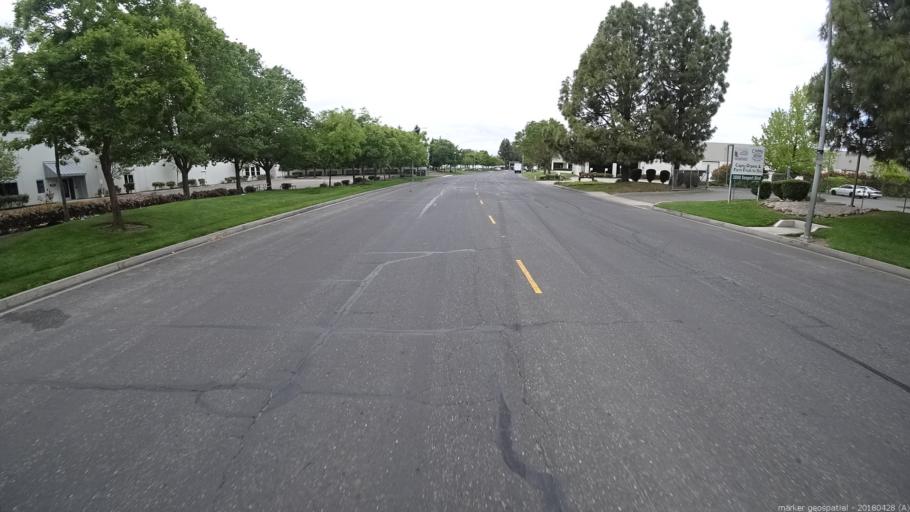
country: US
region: California
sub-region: Yolo County
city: West Sacramento
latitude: 38.5645
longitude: -121.5730
